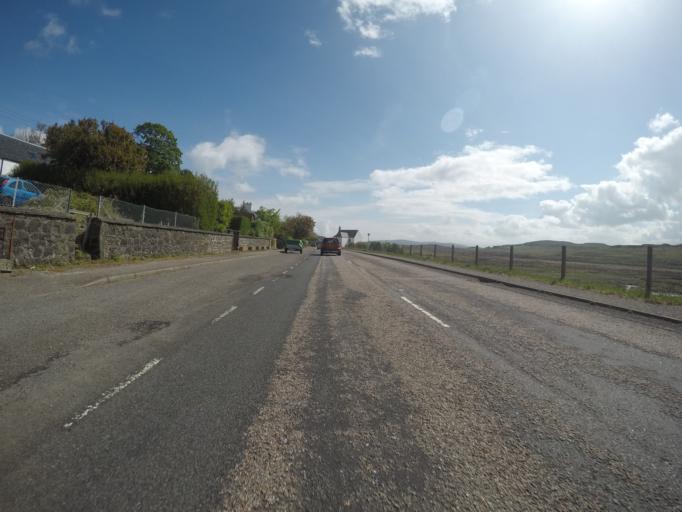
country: GB
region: Scotland
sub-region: Highland
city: Portree
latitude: 57.4837
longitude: -6.3056
